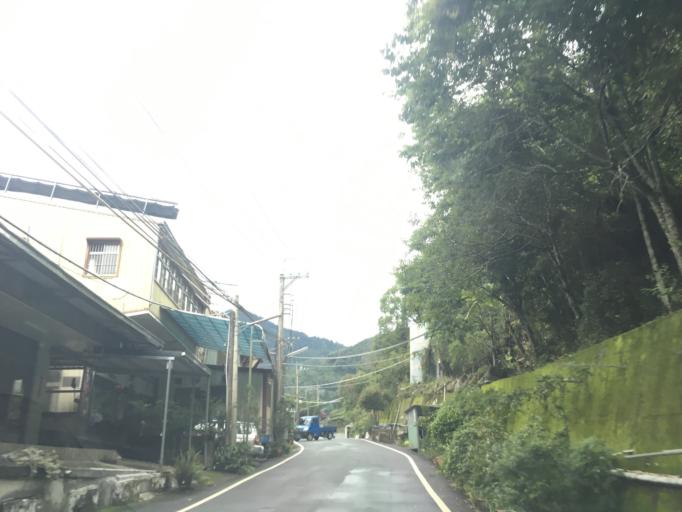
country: TW
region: Taiwan
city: Lugu
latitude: 23.5370
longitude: 120.7115
